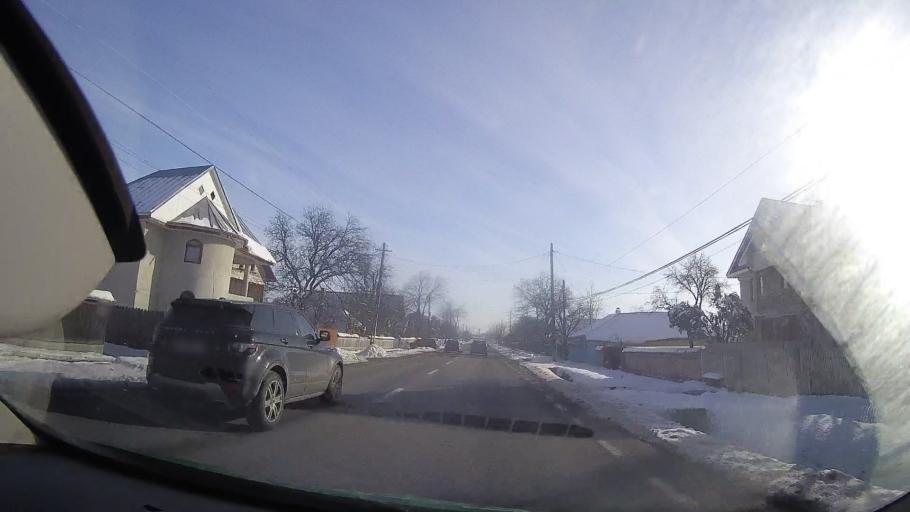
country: RO
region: Neamt
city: Bodesti
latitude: 47.0340
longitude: 26.4135
